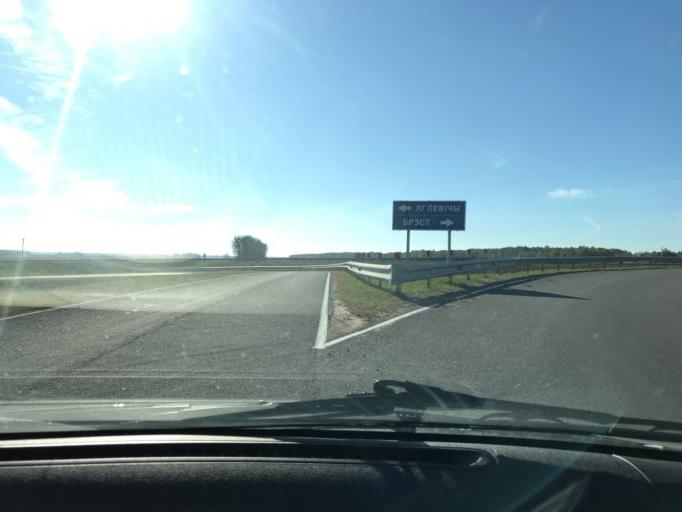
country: BY
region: Brest
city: Ivatsevichy
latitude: 52.6987
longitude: 25.3646
